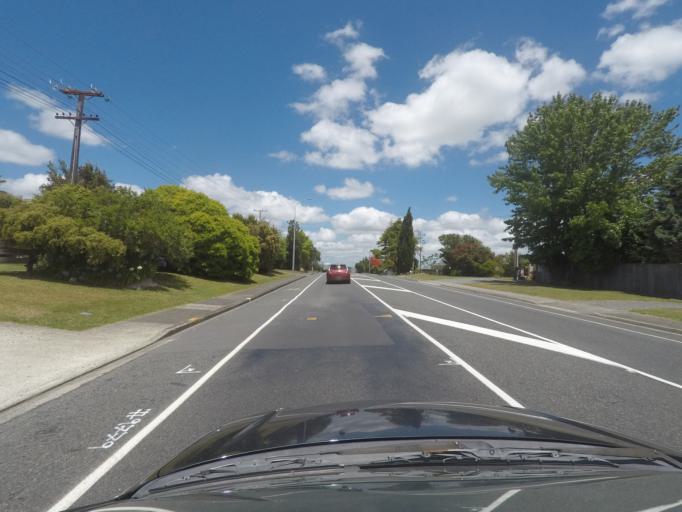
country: NZ
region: Northland
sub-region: Whangarei
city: Whangarei
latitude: -35.7476
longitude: 174.3673
